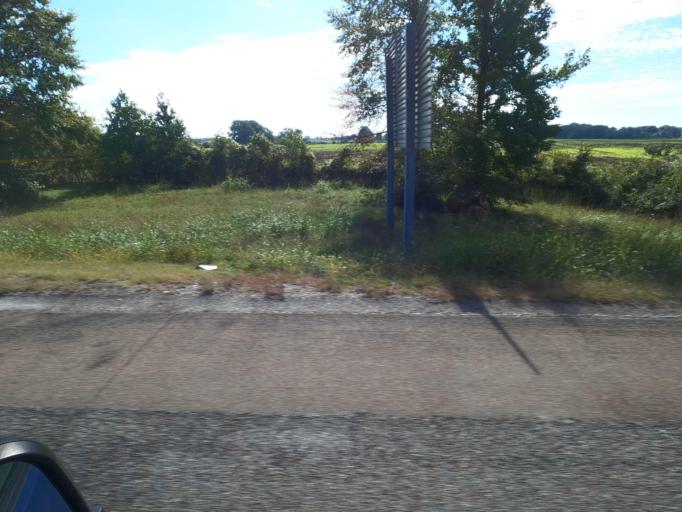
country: US
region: Tennessee
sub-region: Madison County
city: Jackson
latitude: 35.6399
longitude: -88.9253
